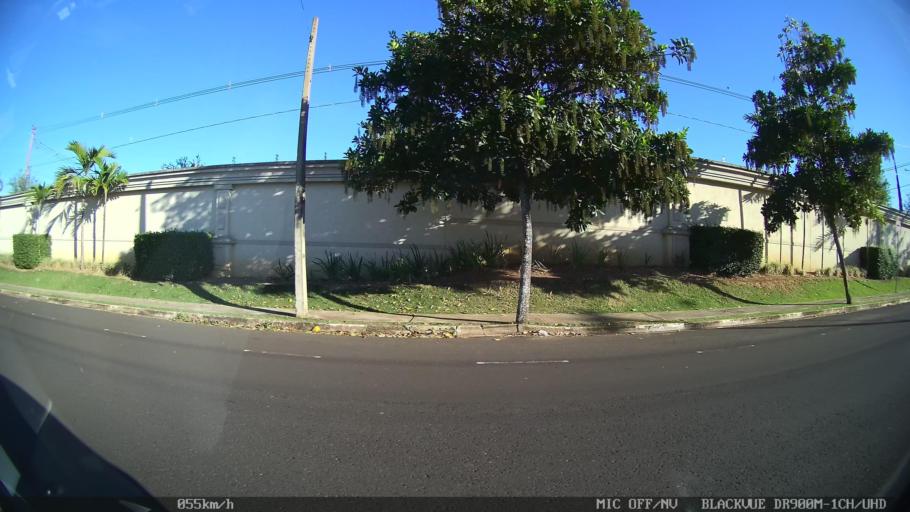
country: BR
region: Sao Paulo
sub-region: Franca
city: Franca
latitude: -20.5711
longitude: -47.4068
